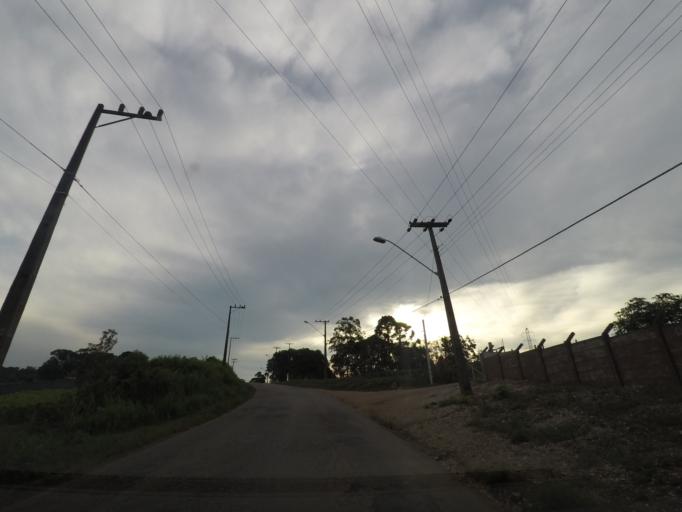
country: BR
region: Parana
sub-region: Colombo
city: Colombo
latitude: -25.2879
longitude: -49.2036
